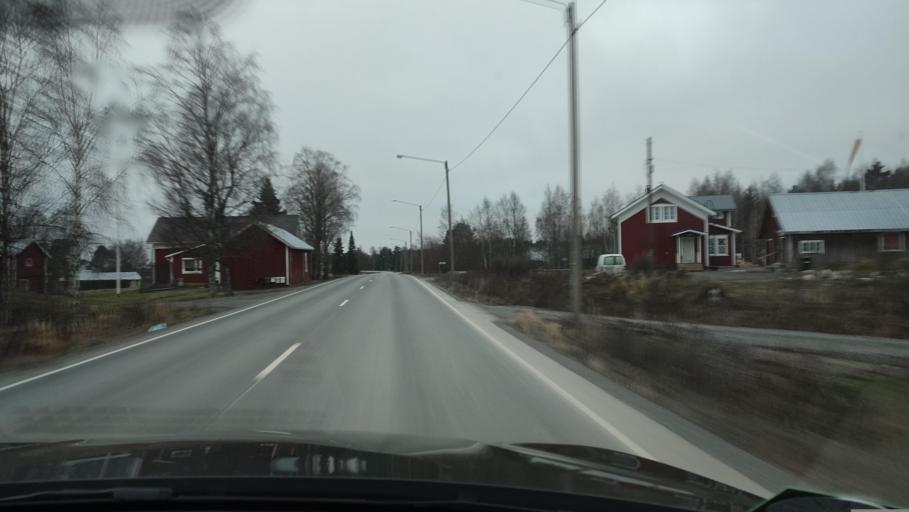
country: FI
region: Southern Ostrobothnia
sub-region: Suupohja
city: Karijoki
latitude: 62.2672
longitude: 21.5494
